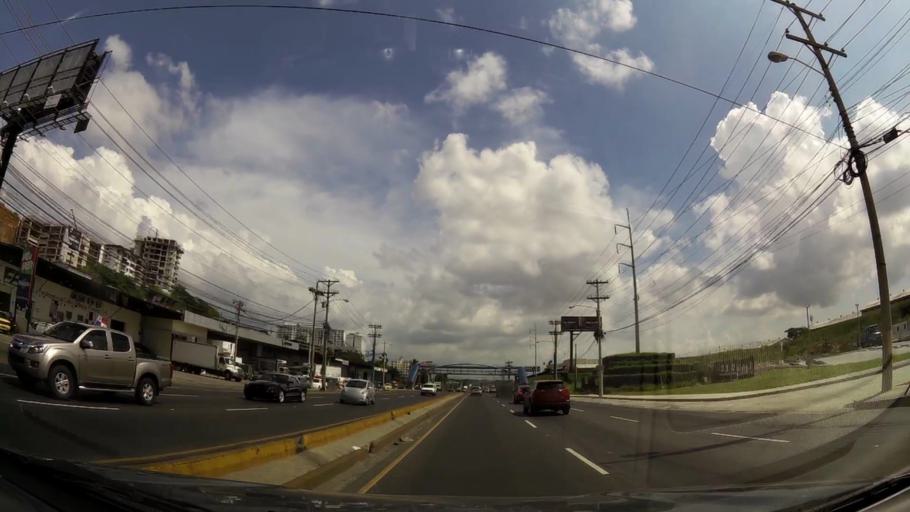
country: PA
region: Panama
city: San Miguelito
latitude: 9.0445
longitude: -79.4704
